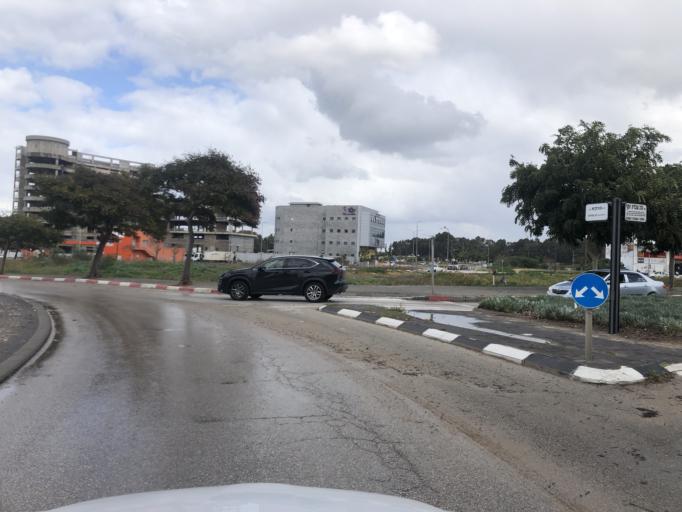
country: IL
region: Central District
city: Bet Yizhaq
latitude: 32.3121
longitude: 34.8728
